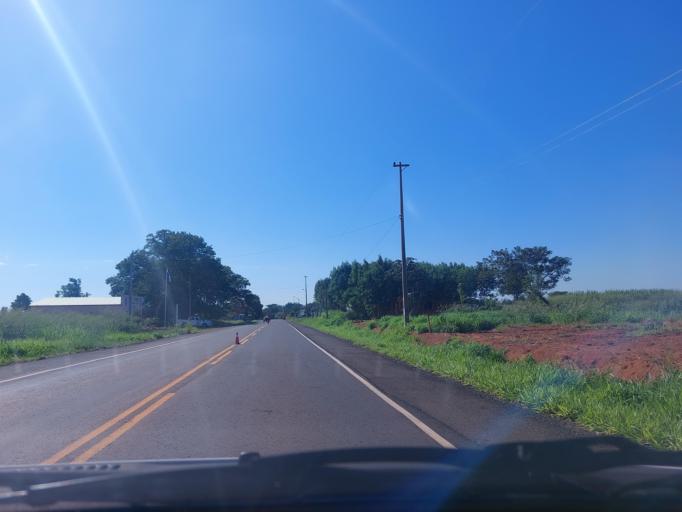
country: PY
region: San Pedro
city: Guayaybi
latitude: -24.3162
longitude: -56.1647
